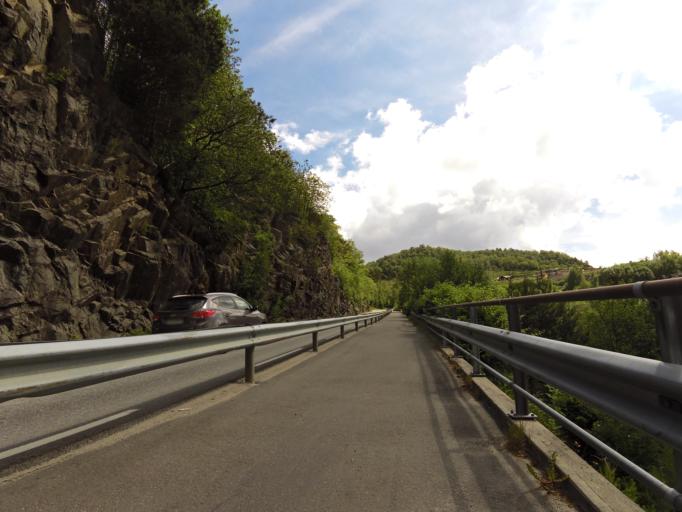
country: NO
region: Vest-Agder
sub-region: Lyngdal
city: Lyngdal
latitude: 58.1176
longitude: 7.0618
